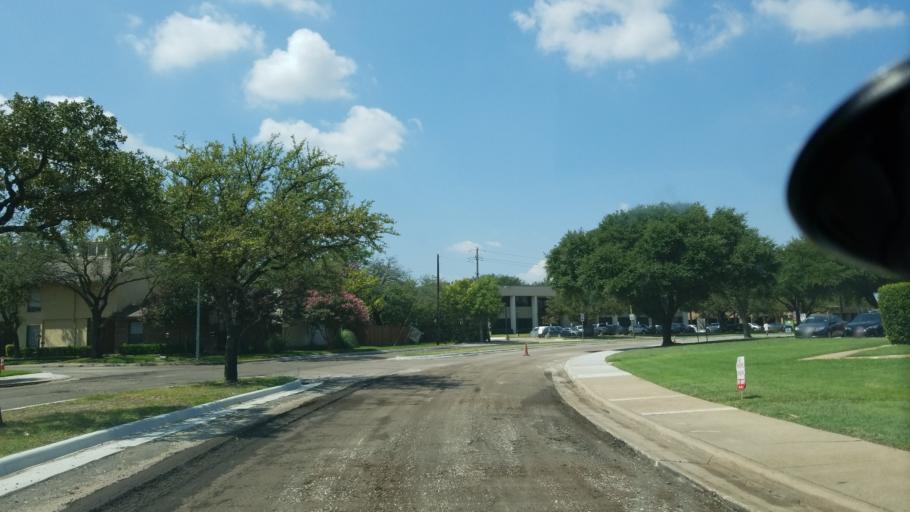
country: US
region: Texas
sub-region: Dallas County
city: Richardson
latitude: 32.9177
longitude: -96.7385
